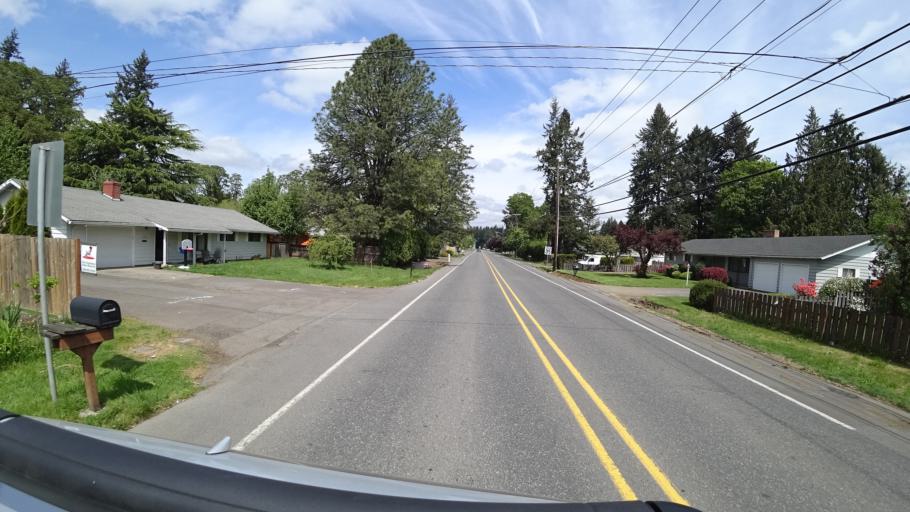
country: US
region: Oregon
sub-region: Washington County
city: Hillsboro
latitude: 45.5292
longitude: -122.9897
